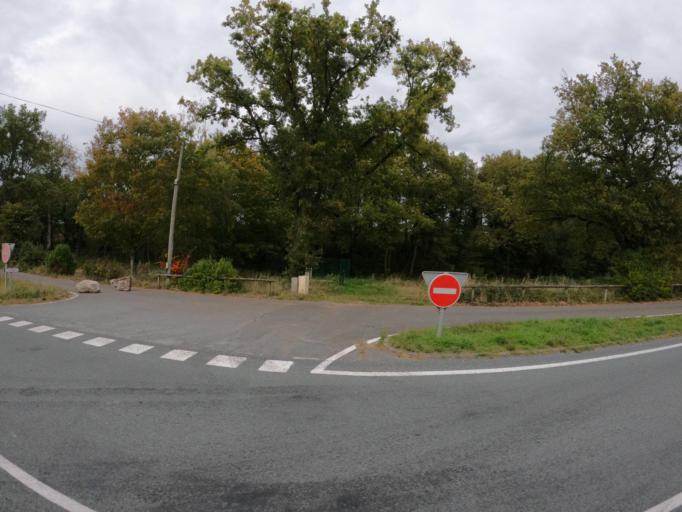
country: FR
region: Pays de la Loire
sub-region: Departement de Maine-et-Loire
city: Torfou
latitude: 47.0333
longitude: -1.0991
